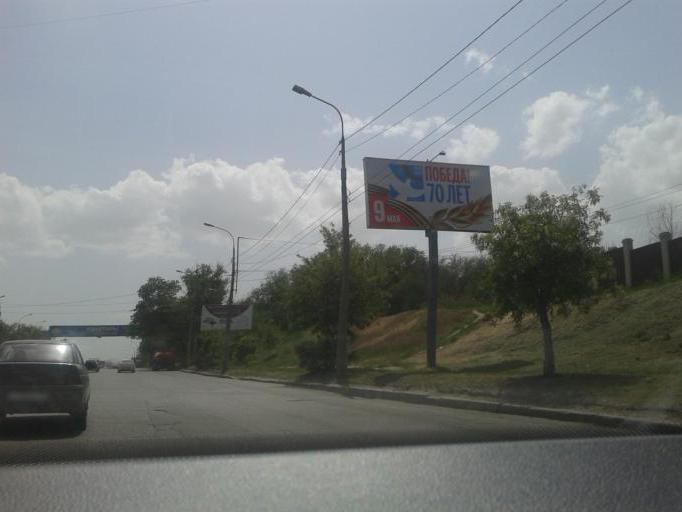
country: RU
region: Volgograd
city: Volgograd
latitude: 48.6795
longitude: 44.4454
